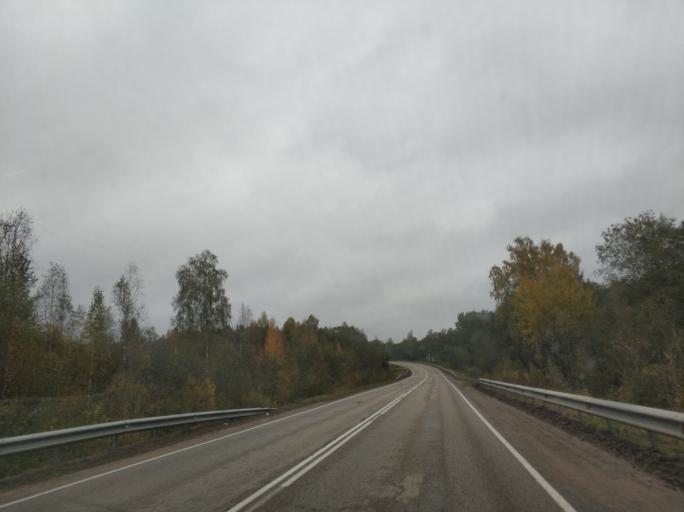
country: BY
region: Vitebsk
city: Rasony
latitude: 56.0590
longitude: 28.7144
